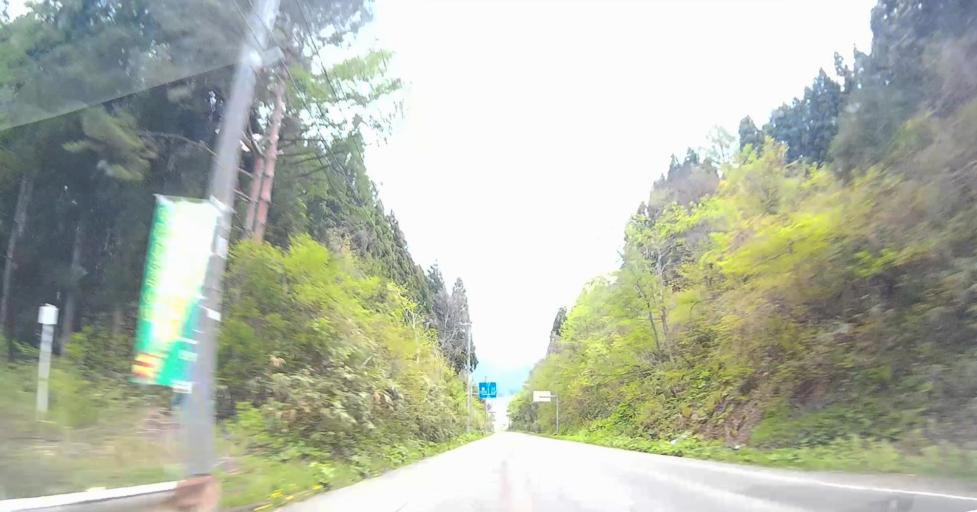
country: JP
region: Aomori
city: Goshogawara
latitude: 41.1769
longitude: 140.4867
